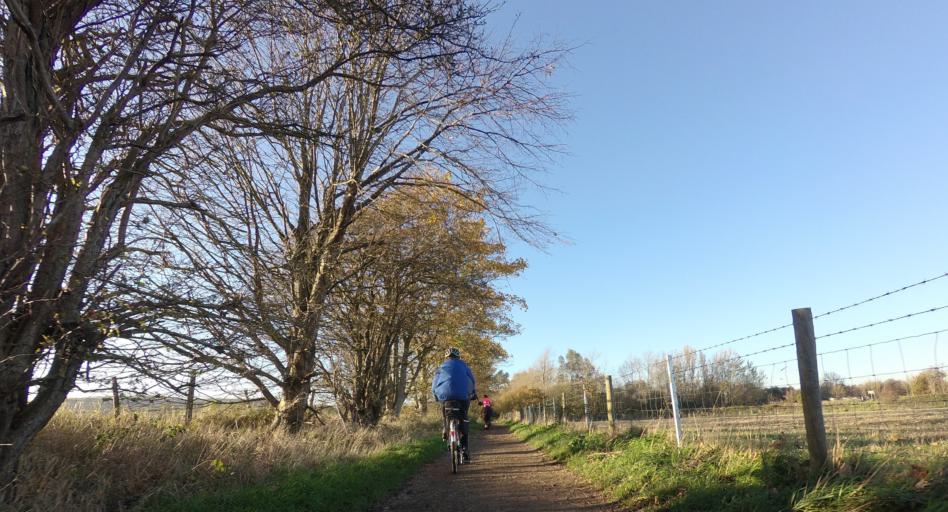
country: GB
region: England
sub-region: West Sussex
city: Steyning
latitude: 50.8775
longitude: -0.3102
